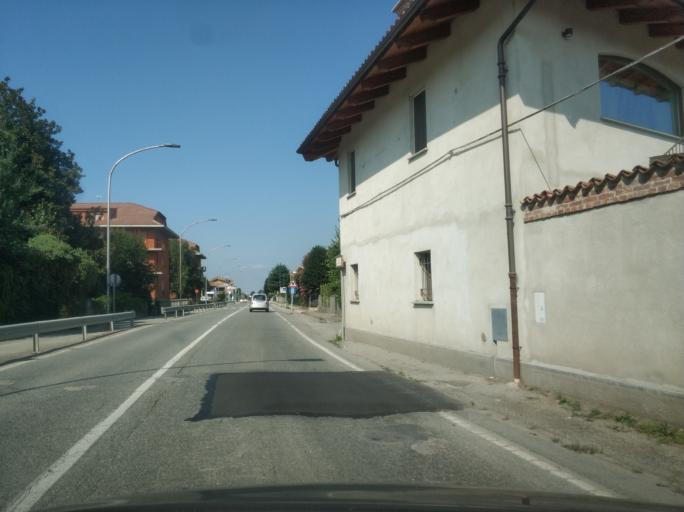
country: IT
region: Piedmont
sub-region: Provincia di Cuneo
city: Centallo
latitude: 44.5033
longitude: 7.5853
